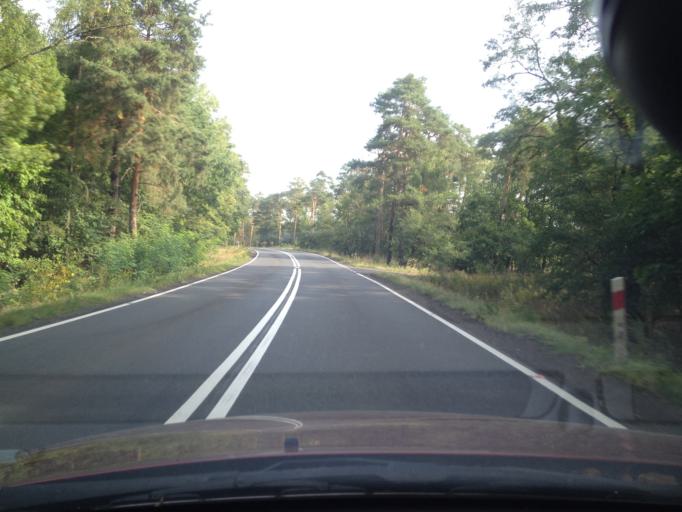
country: PL
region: Lubusz
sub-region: Powiat zaganski
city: Szprotawa
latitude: 51.4594
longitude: 15.6162
